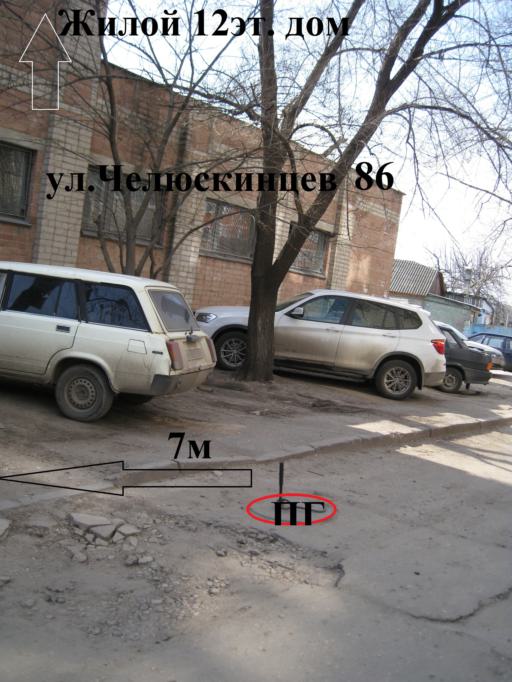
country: RU
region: Voronezj
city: Voronezh
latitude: 51.6483
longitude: 39.1930
